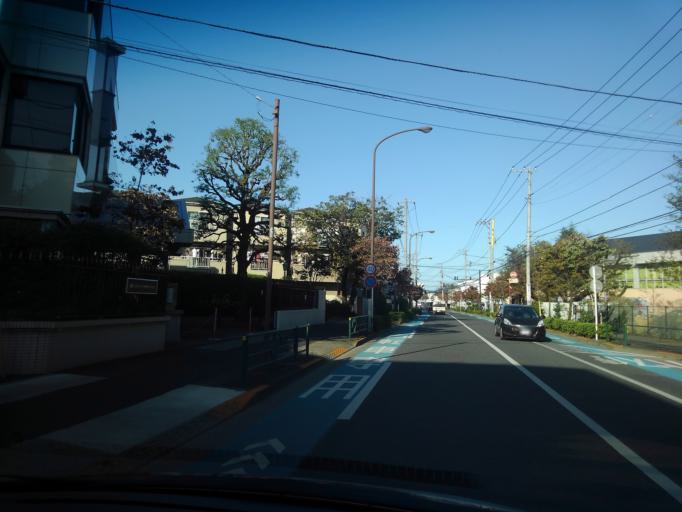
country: JP
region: Tokyo
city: Chofugaoka
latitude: 35.6653
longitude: 139.5340
